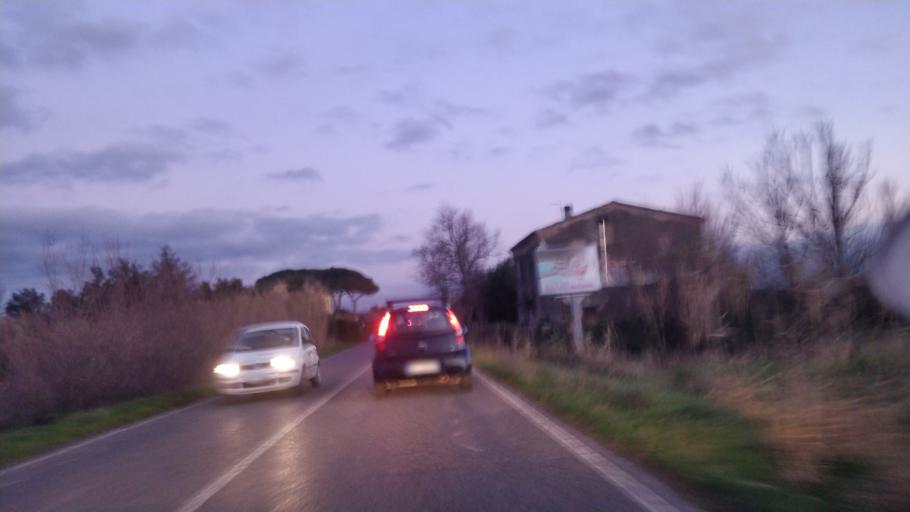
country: IT
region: Tuscany
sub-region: Provincia di Livorno
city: Vada
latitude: 43.3457
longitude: 10.4693
